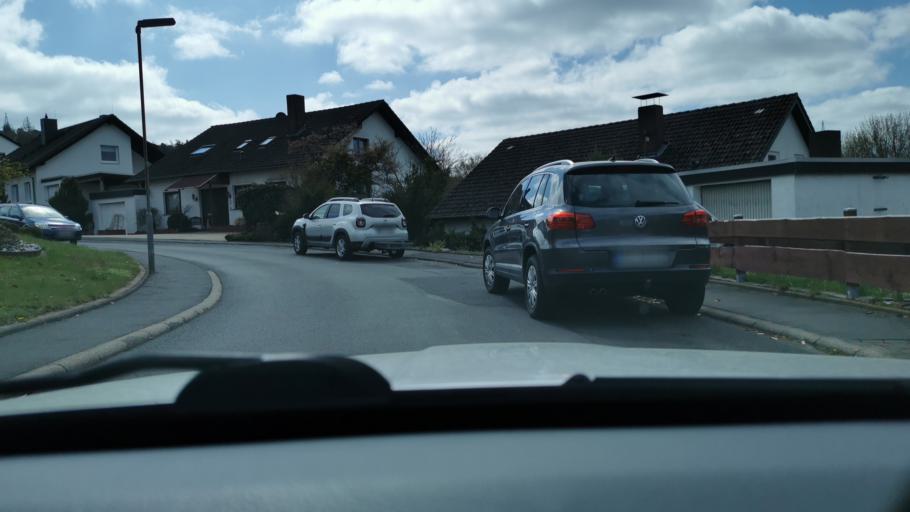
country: DE
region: Hesse
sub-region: Regierungsbezirk Kassel
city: Bad Hersfeld
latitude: 50.8607
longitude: 9.7427
